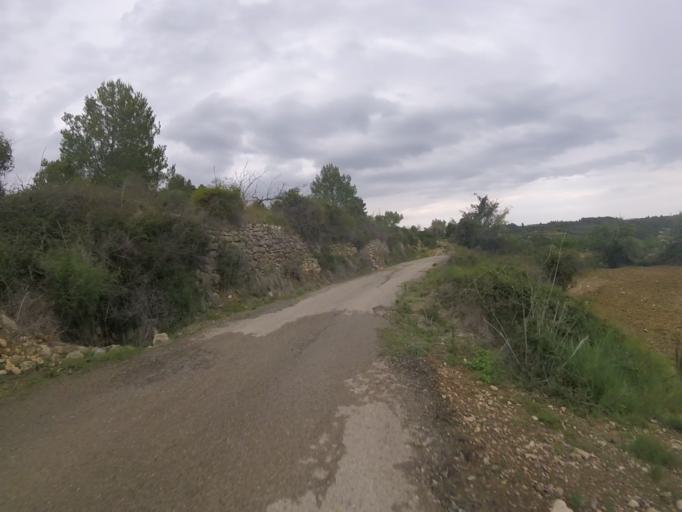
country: ES
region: Valencia
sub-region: Provincia de Castello
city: Sarratella
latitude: 40.2687
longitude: 0.0696
